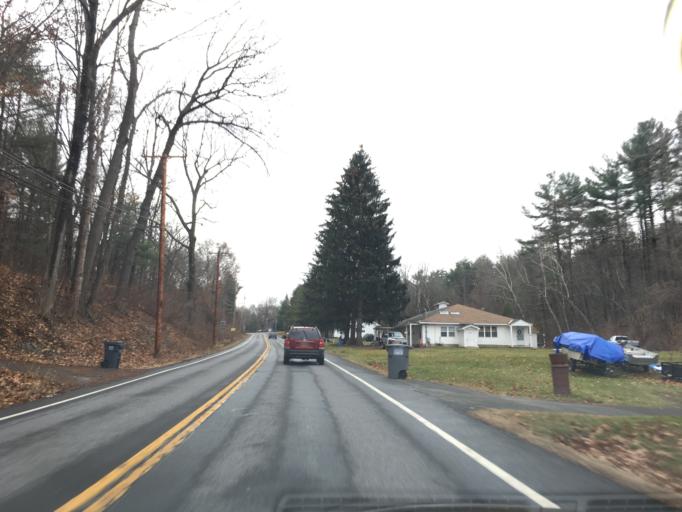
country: US
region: New York
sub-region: Rensselaer County
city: West Sand Lake
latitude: 42.6831
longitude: -73.6066
